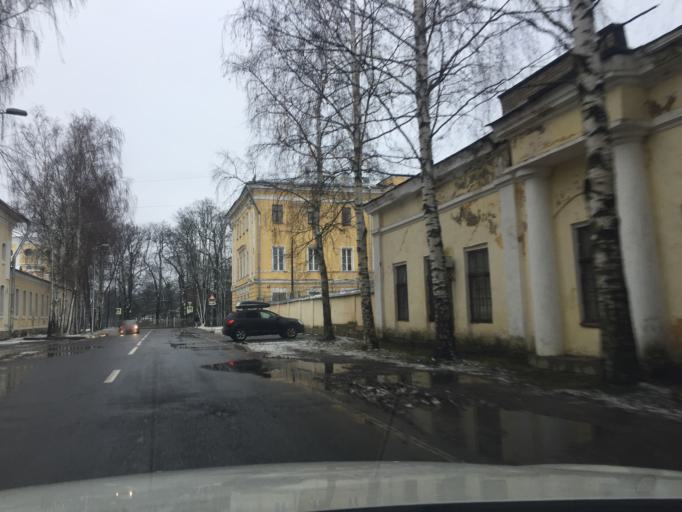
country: RU
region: St.-Petersburg
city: Pushkin
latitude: 59.7077
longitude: 30.3945
